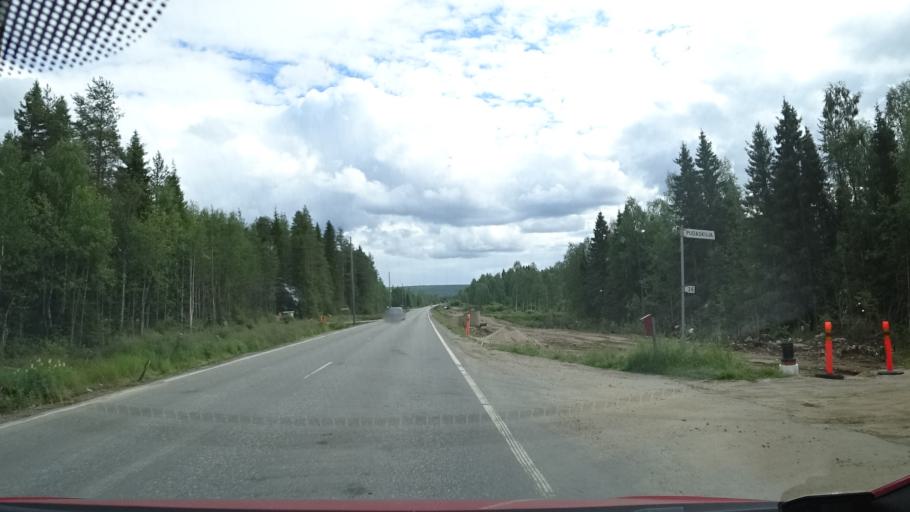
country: FI
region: Lapland
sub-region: Rovaniemi
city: Rovaniemi
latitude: 66.5318
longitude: 25.7352
